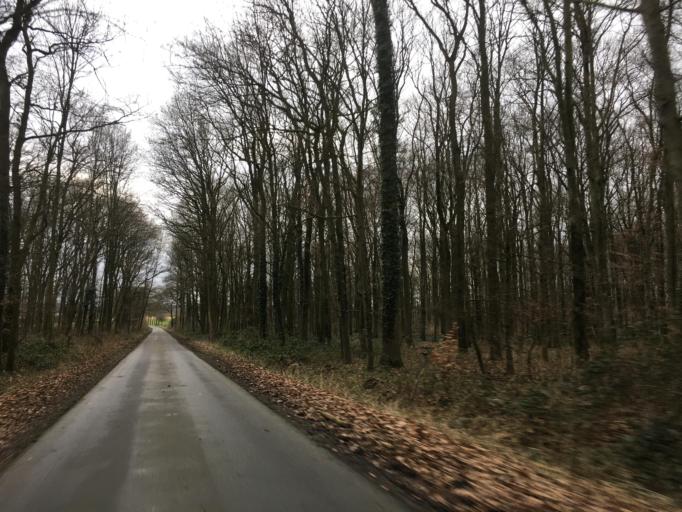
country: DE
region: North Rhine-Westphalia
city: Ludinghausen
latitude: 51.7990
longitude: 7.4598
